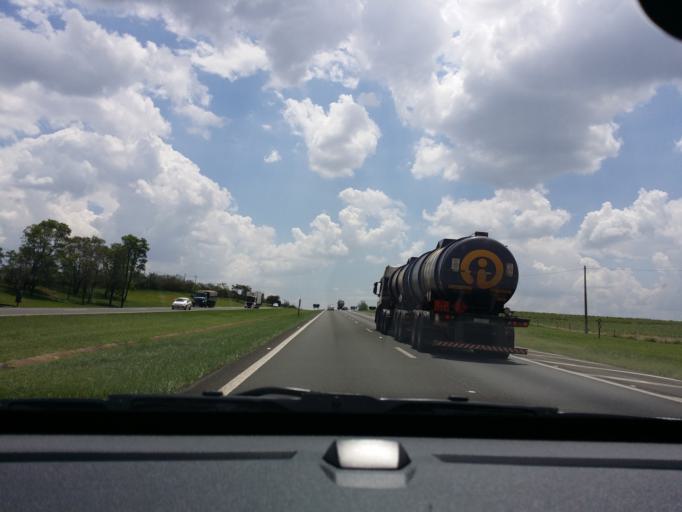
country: BR
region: Sao Paulo
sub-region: Itirapina
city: Itirapina
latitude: -22.2143
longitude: -47.7671
